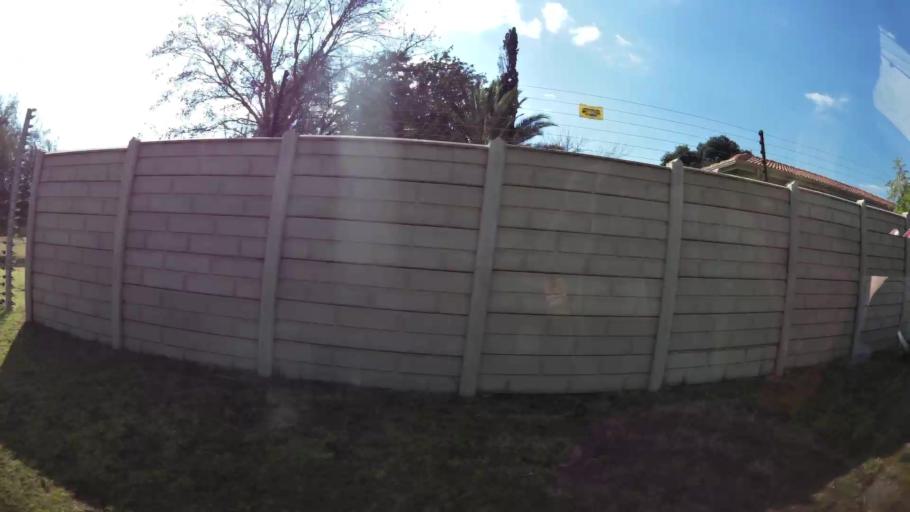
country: ZA
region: Gauteng
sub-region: Ekurhuleni Metropolitan Municipality
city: Benoni
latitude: -26.0896
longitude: 28.3302
